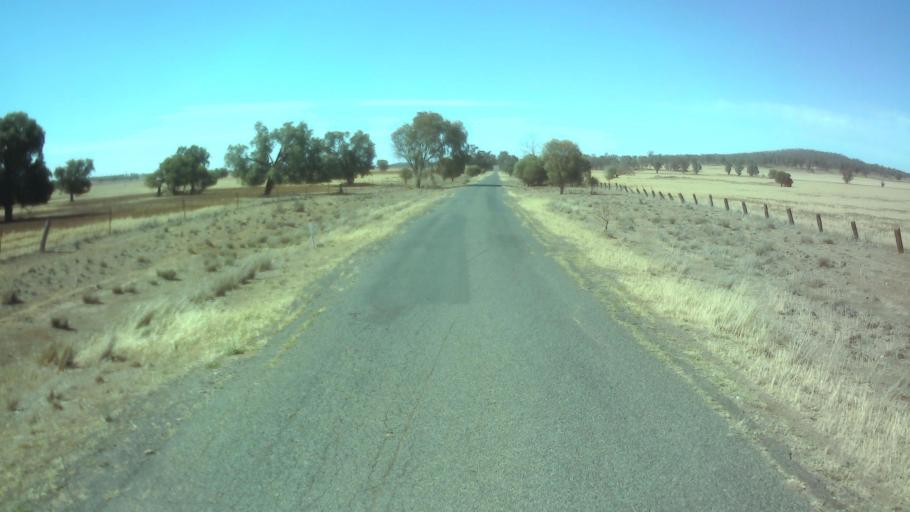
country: AU
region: New South Wales
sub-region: Forbes
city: Forbes
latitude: -33.7418
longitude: 147.7405
